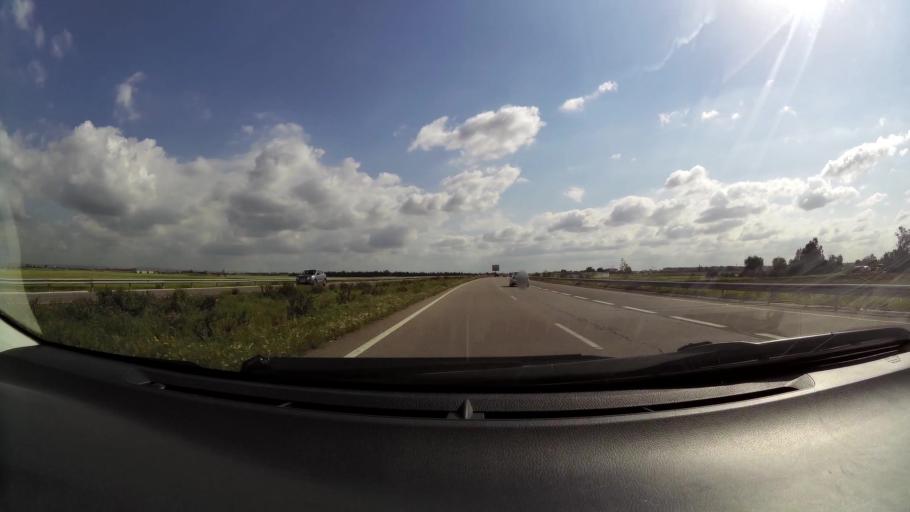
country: MA
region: Chaouia-Ouardigha
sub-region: Settat Province
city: Berrechid
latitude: 33.2692
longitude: -7.5492
